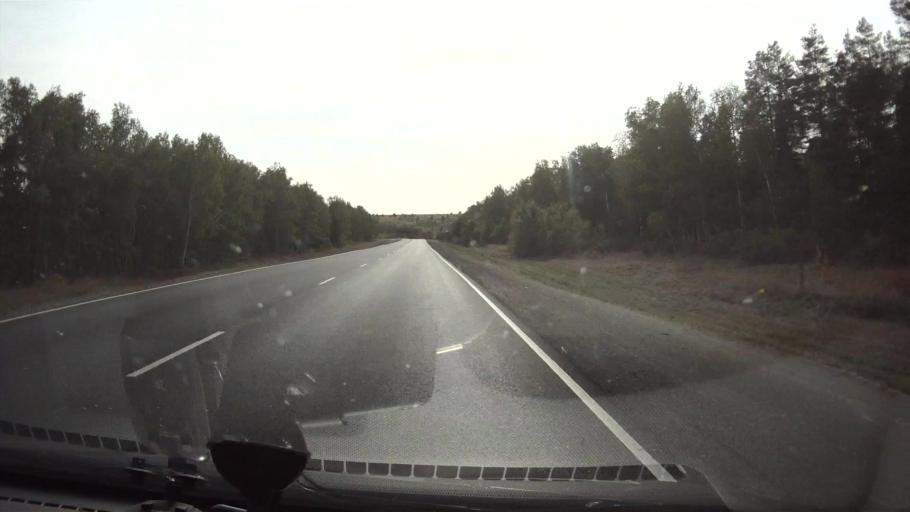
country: RU
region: Saratov
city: Sennoy
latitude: 52.1044
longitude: 46.8183
